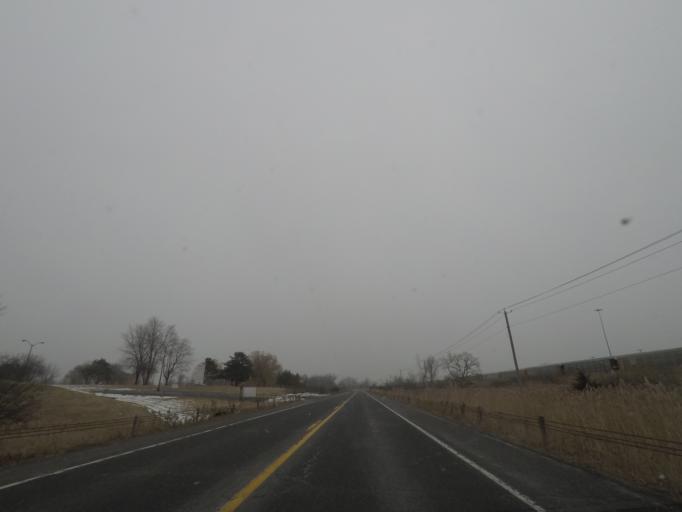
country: US
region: New York
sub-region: Albany County
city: Delmar
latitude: 42.5710
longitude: -73.8563
